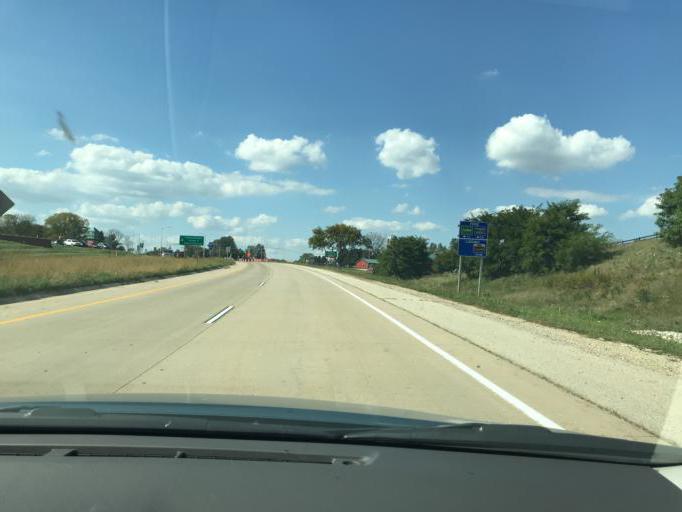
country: US
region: Wisconsin
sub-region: Walworth County
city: Williams Bay
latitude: 42.5984
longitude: -88.5383
